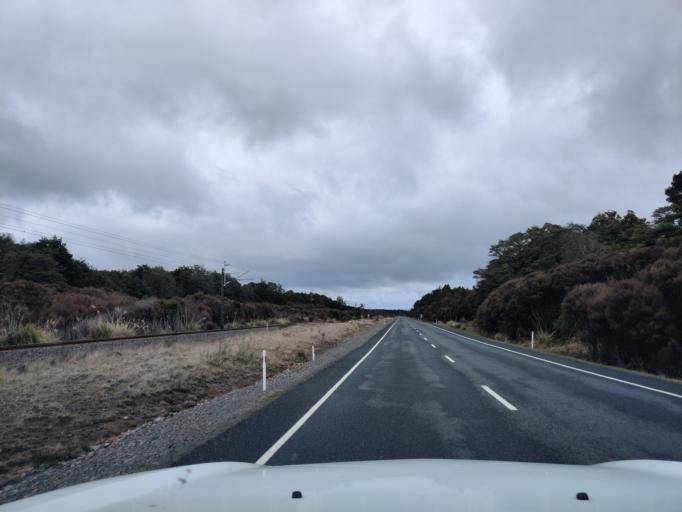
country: NZ
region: Manawatu-Wanganui
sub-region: Ruapehu District
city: Waiouru
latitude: -39.3143
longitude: 175.3879
